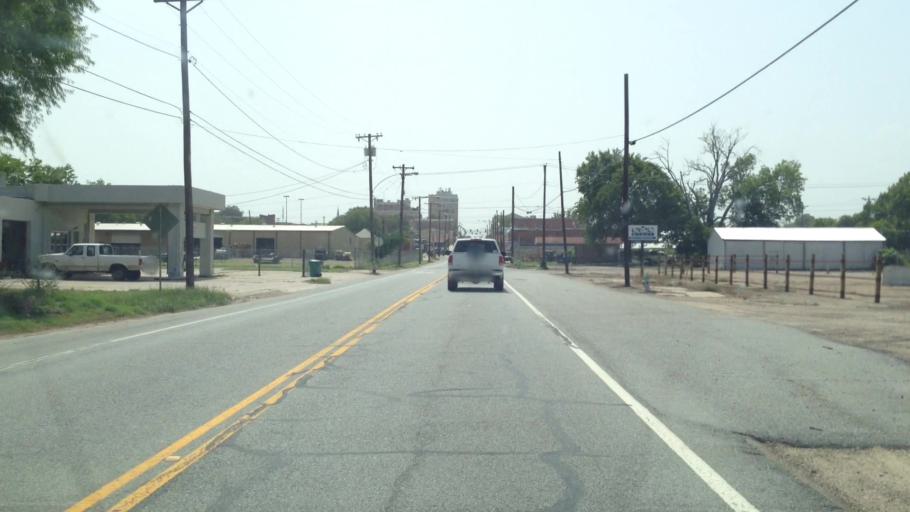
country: US
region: Texas
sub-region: Hunt County
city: Greenville
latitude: 33.1398
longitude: -96.1013
